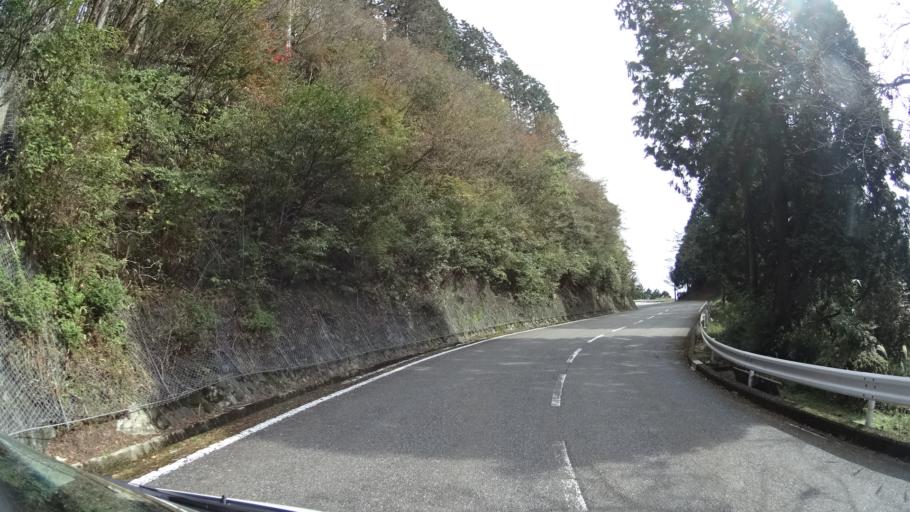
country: JP
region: Shiga Prefecture
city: Otsu-shi
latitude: 35.0649
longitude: 135.8348
